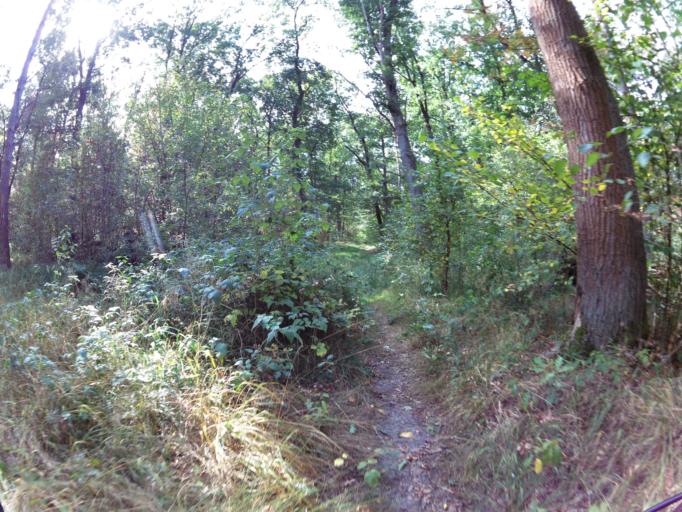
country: DE
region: North Rhine-Westphalia
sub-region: Regierungsbezirk Koln
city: Gangelt
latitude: 50.9651
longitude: 6.0148
